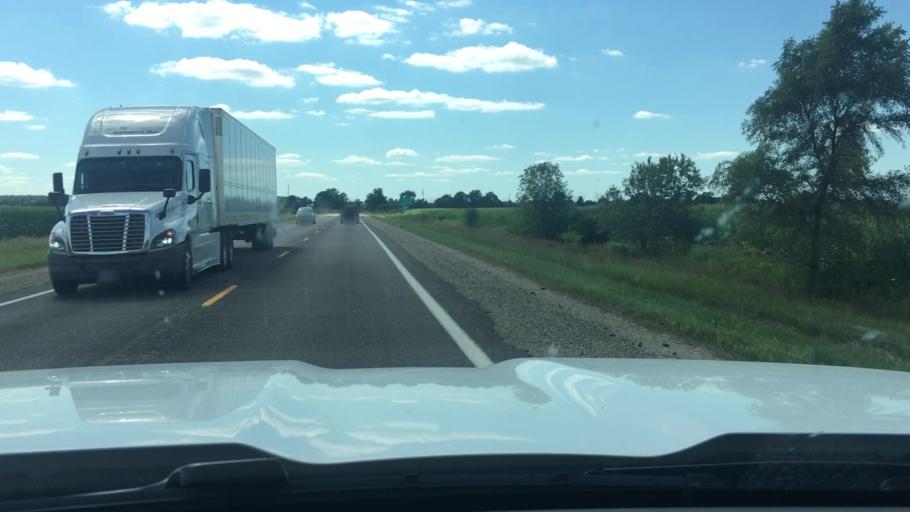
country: US
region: Michigan
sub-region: Gratiot County
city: Ithaca
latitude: 43.1758
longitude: -84.4733
